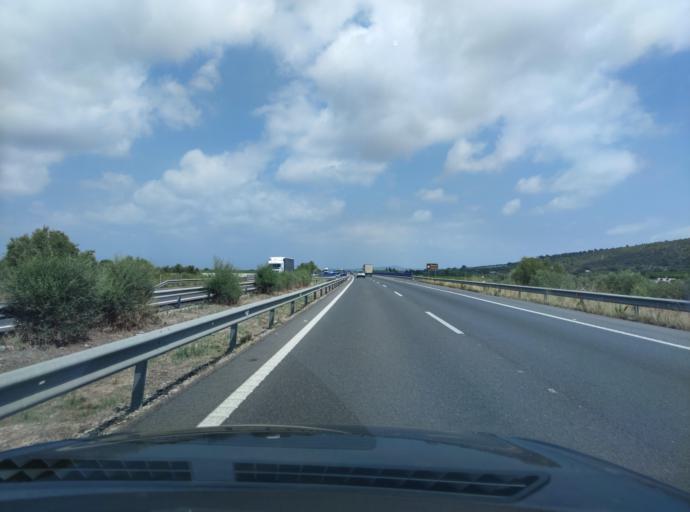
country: ES
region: Valencia
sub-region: Provincia de Castello
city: Vinaros
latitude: 40.5001
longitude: 0.4160
